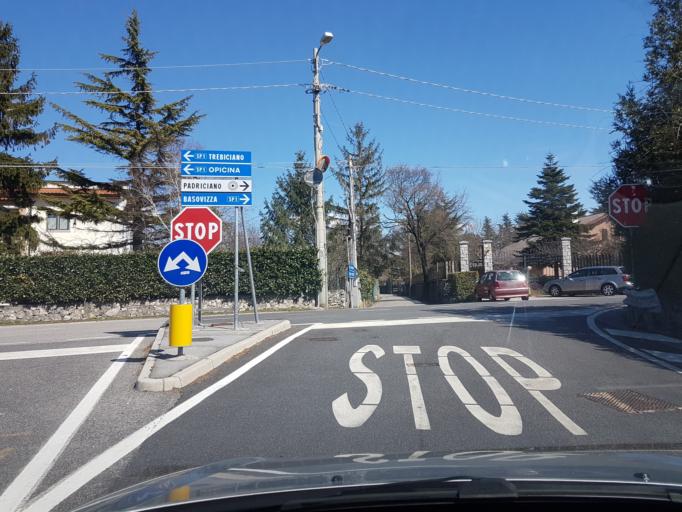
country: IT
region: Friuli Venezia Giulia
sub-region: Provincia di Trieste
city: Trieste
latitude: 45.6608
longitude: 13.8361
